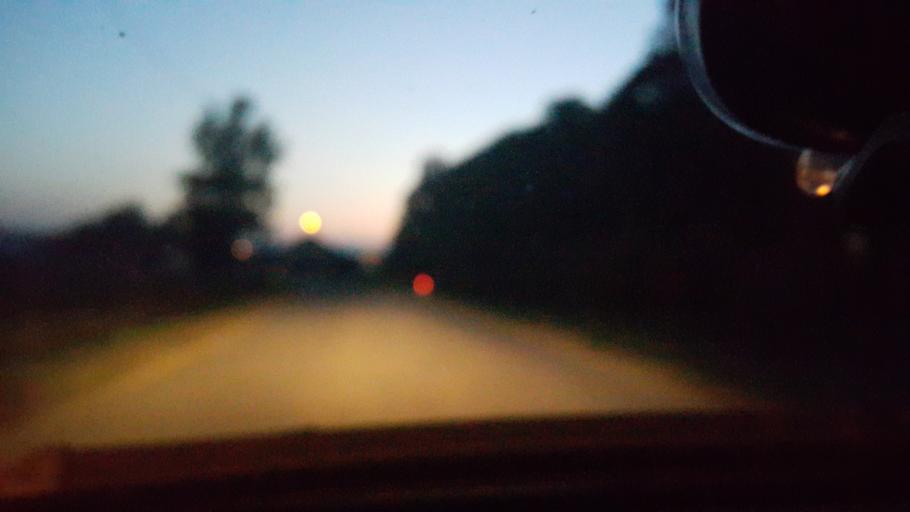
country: SI
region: Miklavz na Dravskem Polju
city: Miklavz na Dravskem Polju
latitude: 46.5396
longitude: 15.6955
